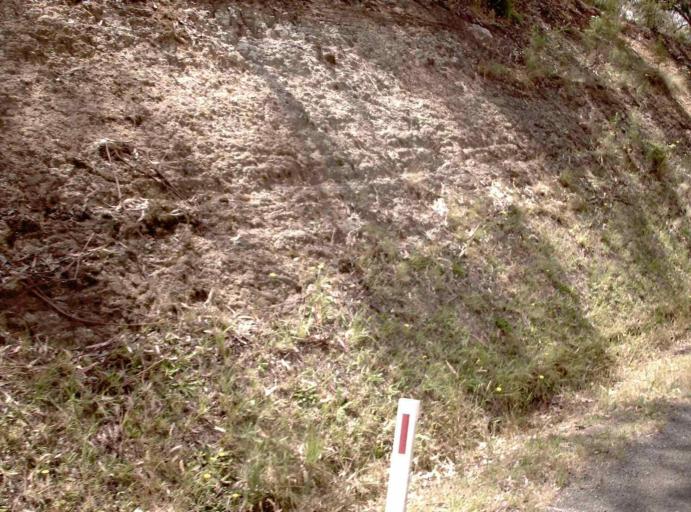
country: AU
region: Victoria
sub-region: Latrobe
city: Traralgon
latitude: -38.3609
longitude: 146.7565
